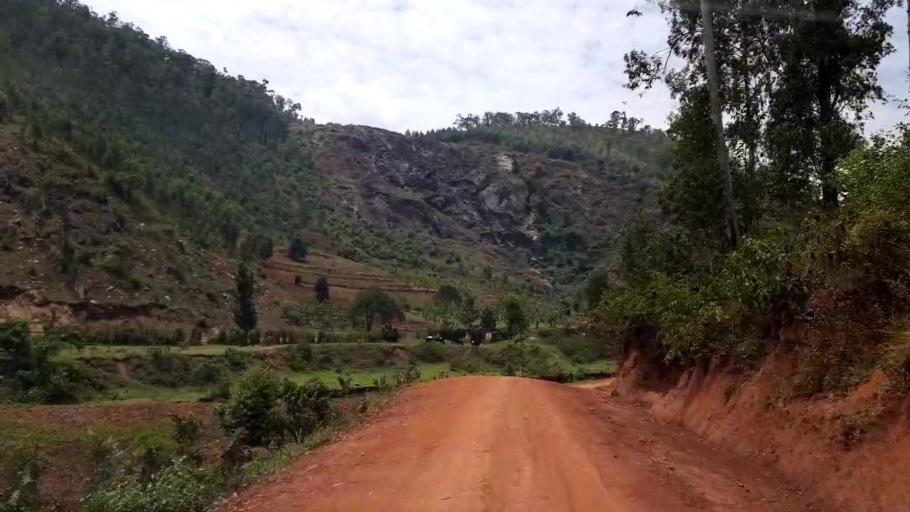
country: RW
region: Northern Province
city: Byumba
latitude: -1.5128
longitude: 30.1933
